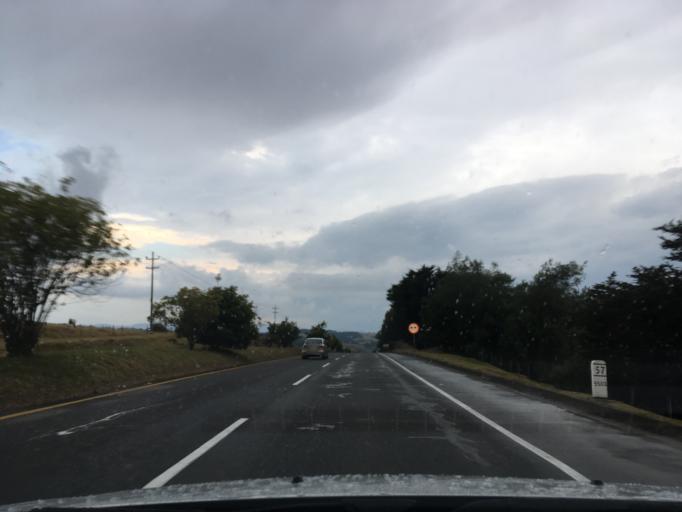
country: CO
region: Cundinamarca
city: Choconta
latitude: 5.1205
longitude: -73.6962
